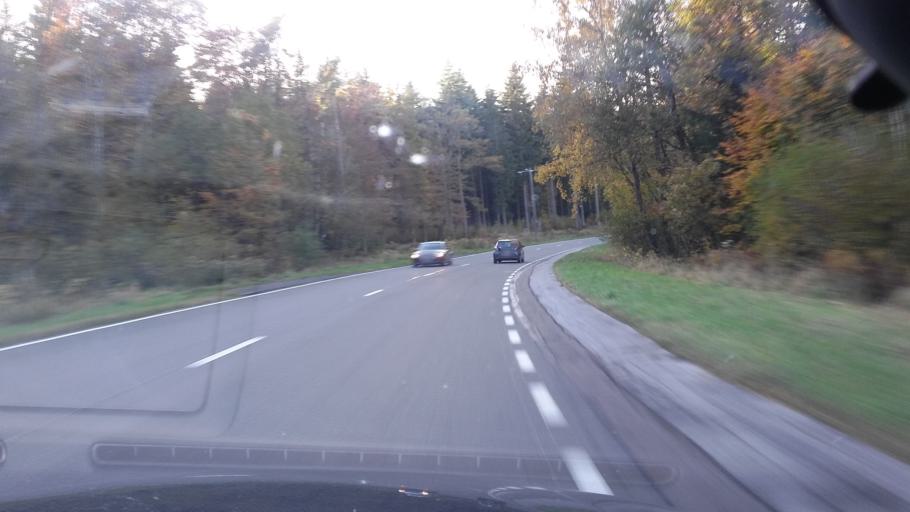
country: BE
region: Wallonia
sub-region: Province du Luxembourg
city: Bouillon
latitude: 49.7588
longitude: 5.1404
